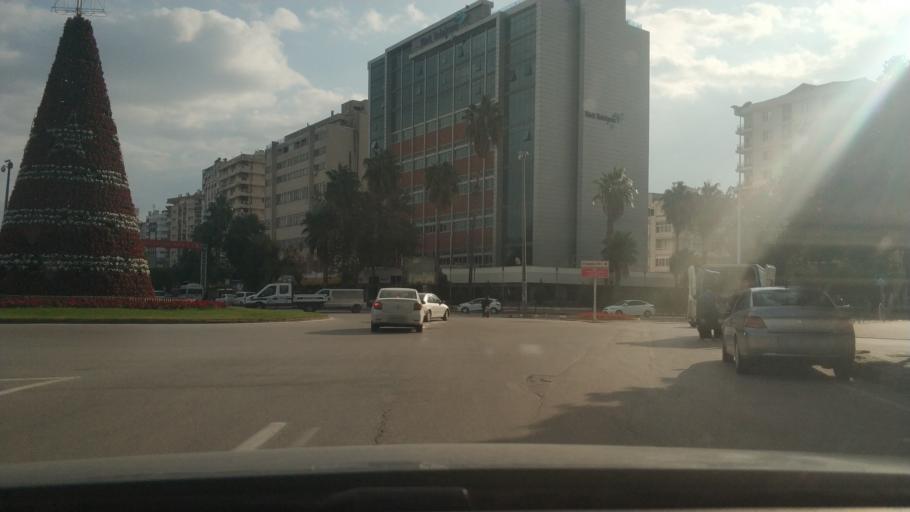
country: TR
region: Adana
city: Adana
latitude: 37.0029
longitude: 35.3190
